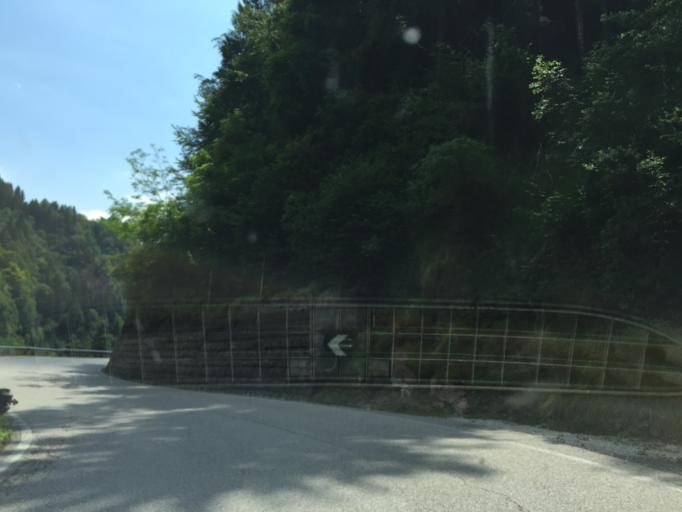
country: IT
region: Veneto
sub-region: Provincia di Belluno
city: Lamon
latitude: 46.0546
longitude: 11.7624
